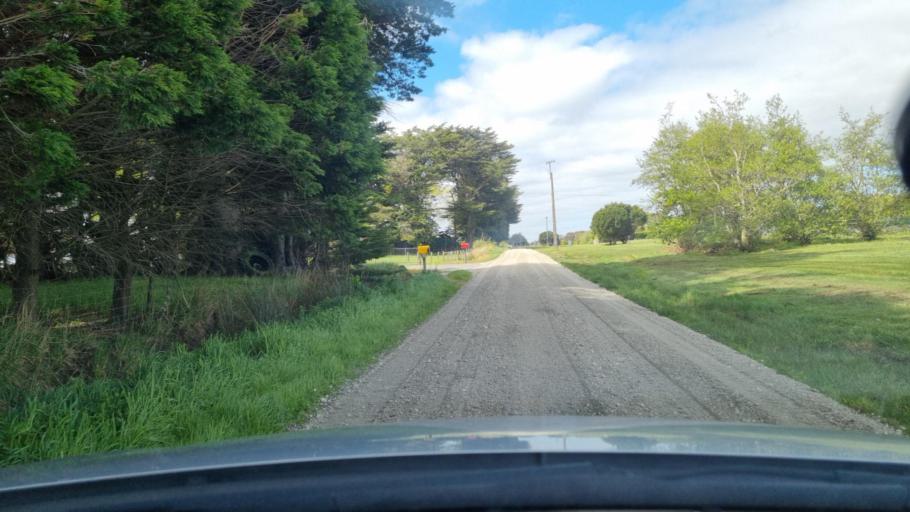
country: NZ
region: Southland
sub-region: Invercargill City
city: Invercargill
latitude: -46.4408
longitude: 168.3882
